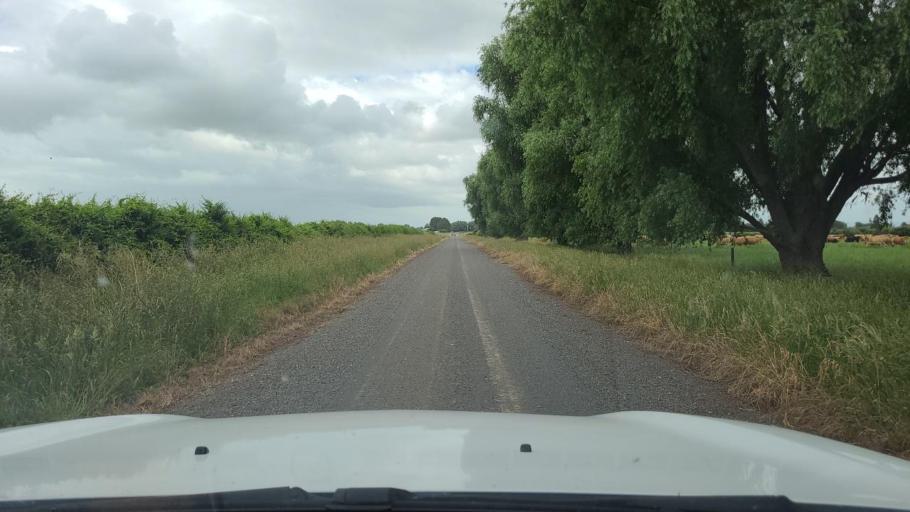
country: NZ
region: Bay of Plenty
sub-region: Western Bay of Plenty District
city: Katikati
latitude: -37.5891
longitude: 175.7132
